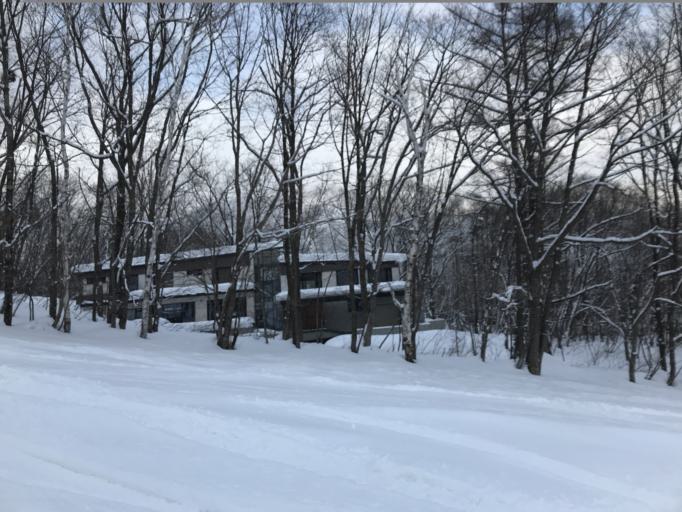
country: JP
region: Nagano
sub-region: Kitaazumi Gun
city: Hakuba
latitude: 36.7120
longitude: 137.8290
